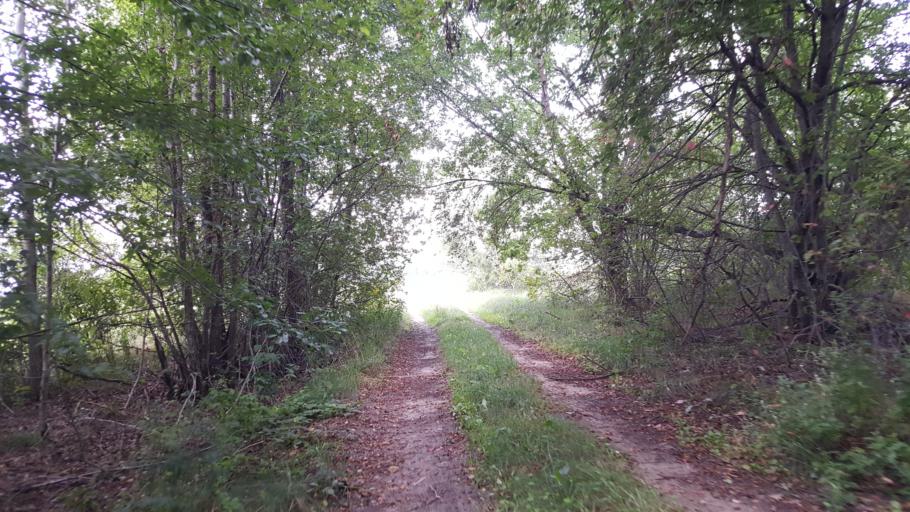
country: PL
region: Podlasie
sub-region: Powiat hajnowski
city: Hajnowka
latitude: 52.5694
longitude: 23.6014
